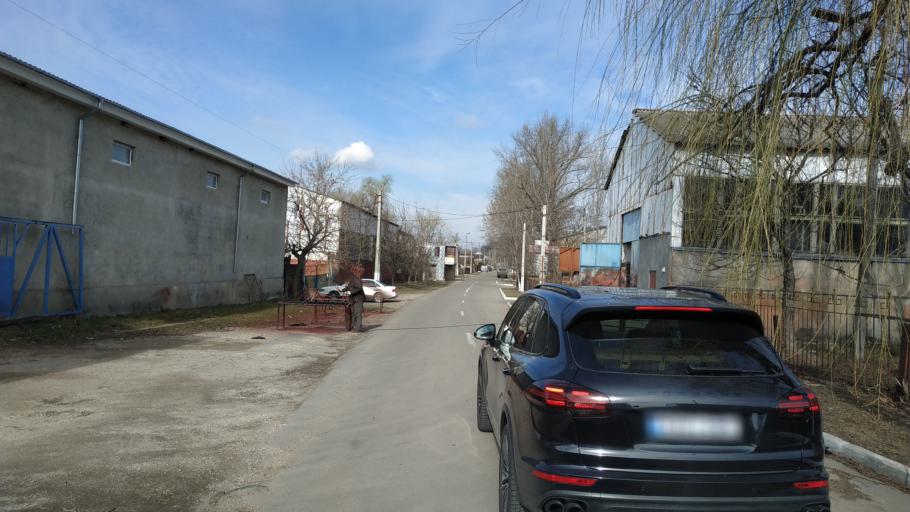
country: MD
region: Hincesti
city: Hincesti
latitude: 46.8288
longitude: 28.6058
